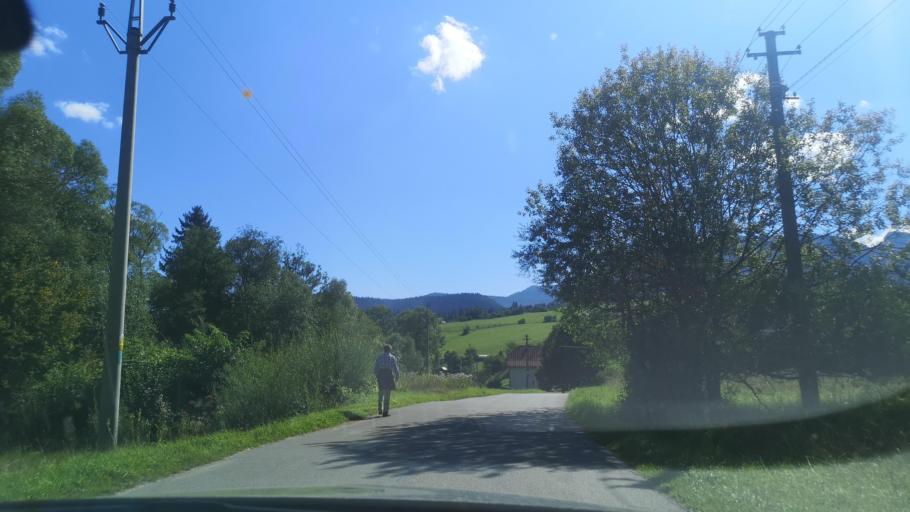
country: SK
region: Zilinsky
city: Oravska Lesna
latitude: 49.2799
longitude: 19.1335
